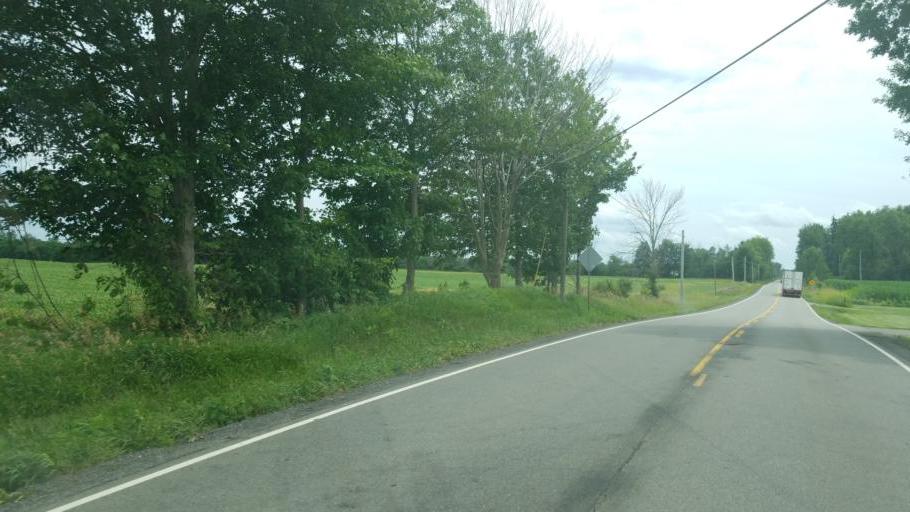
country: US
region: Ohio
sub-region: Licking County
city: Utica
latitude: 40.2801
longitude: -82.5149
